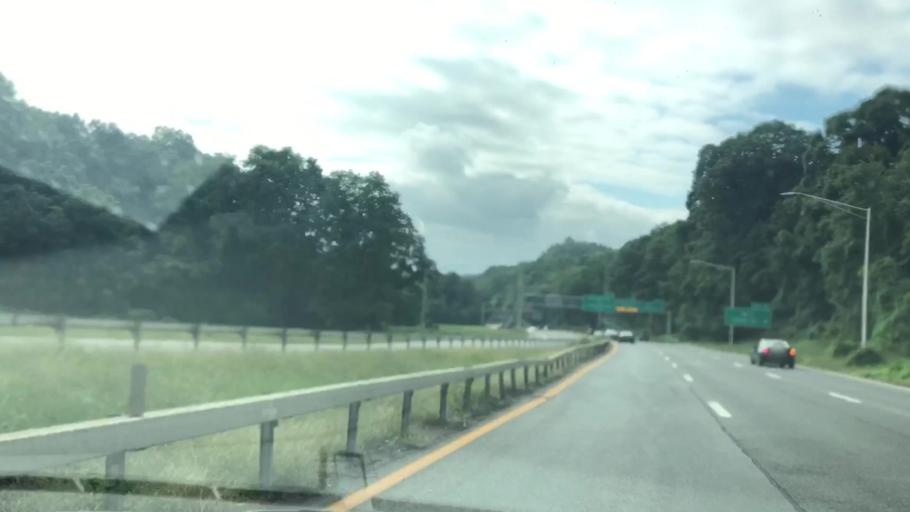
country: US
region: New York
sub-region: Westchester County
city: Yonkers
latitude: 40.9374
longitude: -73.8774
